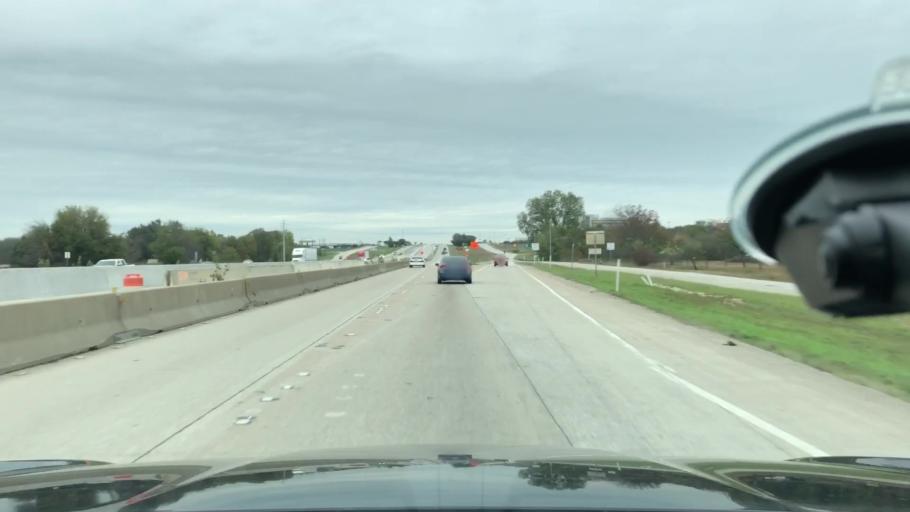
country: US
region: Texas
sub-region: Ellis County
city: Waxahachie
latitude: 32.4203
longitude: -96.8677
